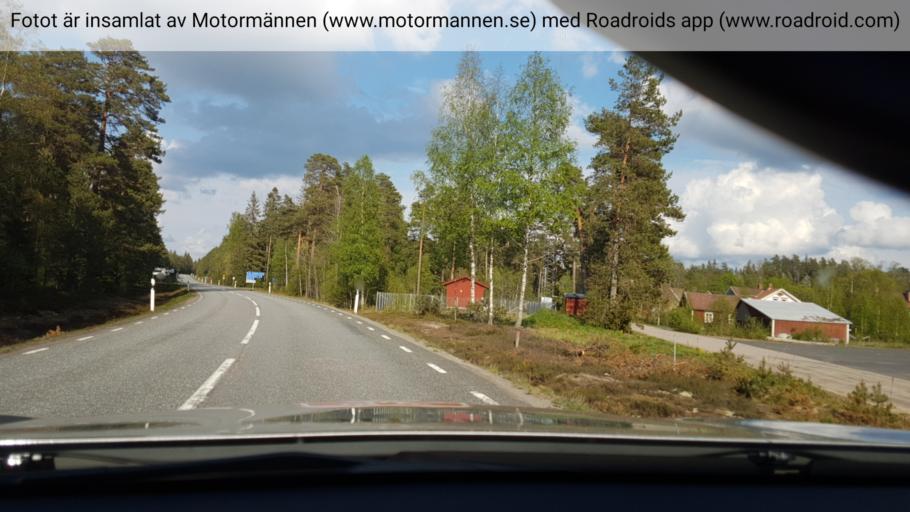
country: SE
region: Joenkoeping
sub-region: Vaggeryds Kommun
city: Skillingaryd
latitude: 57.3836
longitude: 13.9911
